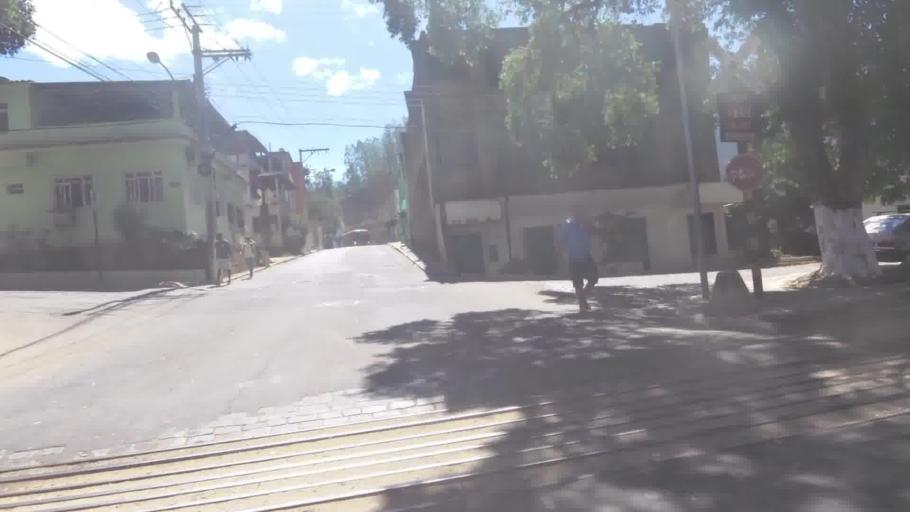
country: BR
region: Espirito Santo
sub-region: Cachoeiro De Itapemirim
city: Cachoeiro de Itapemirim
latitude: -20.9138
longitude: -41.1954
